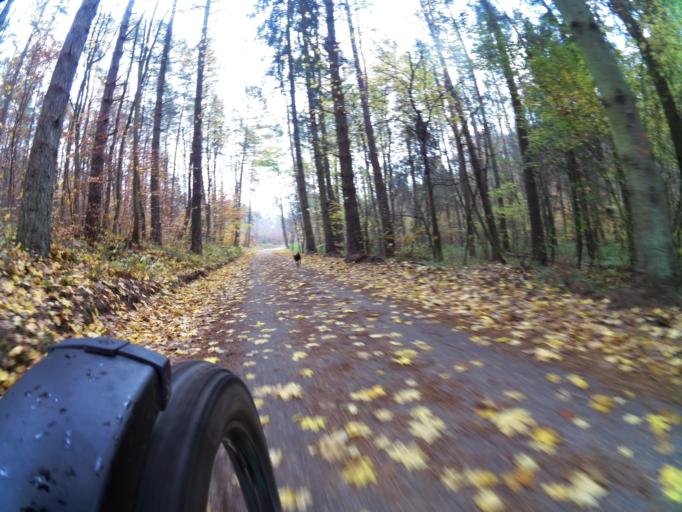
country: PL
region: Pomeranian Voivodeship
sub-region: Powiat pucki
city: Krokowa
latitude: 54.7801
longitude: 18.0908
